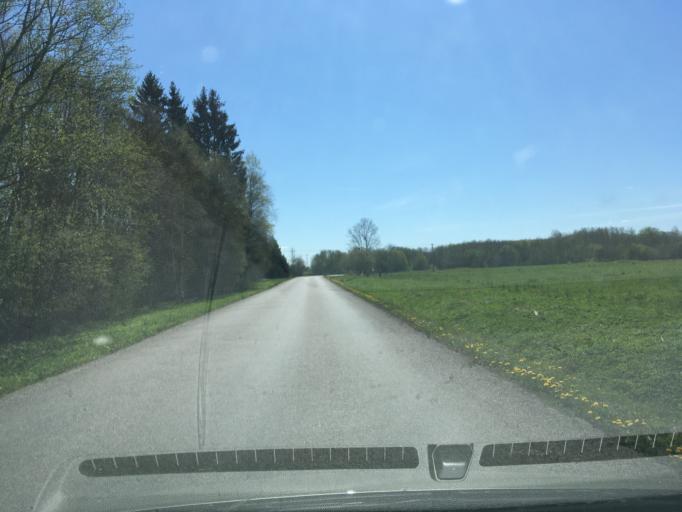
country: EE
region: Harju
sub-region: Raasiku vald
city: Arukula
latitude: 59.4074
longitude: 25.0776
